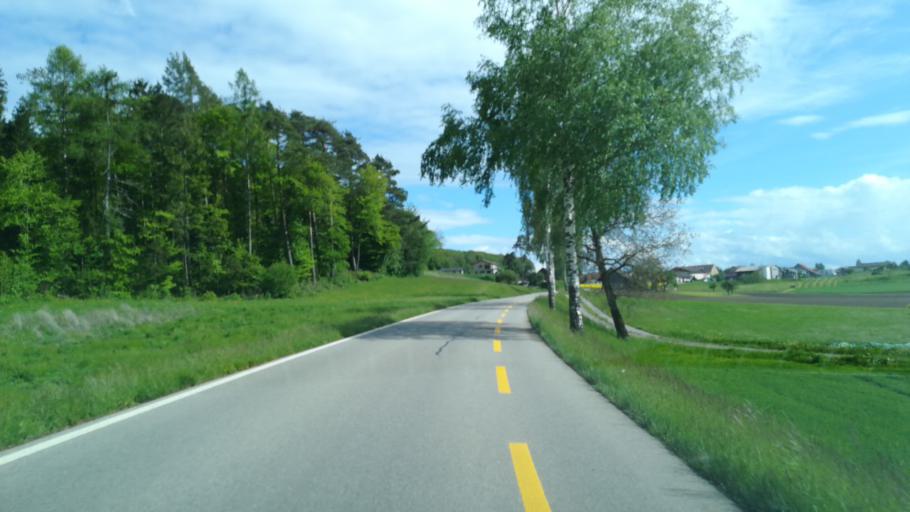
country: CH
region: Schaffhausen
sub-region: Bezirk Reiat
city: Thayngen
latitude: 47.7175
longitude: 8.7217
